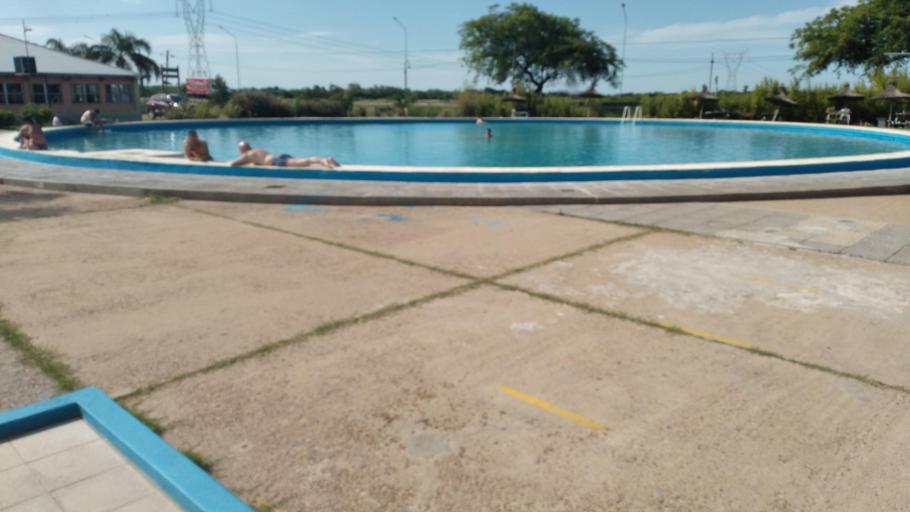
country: AR
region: Entre Rios
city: Gualeguaychu
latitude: -33.0171
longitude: -58.4807
